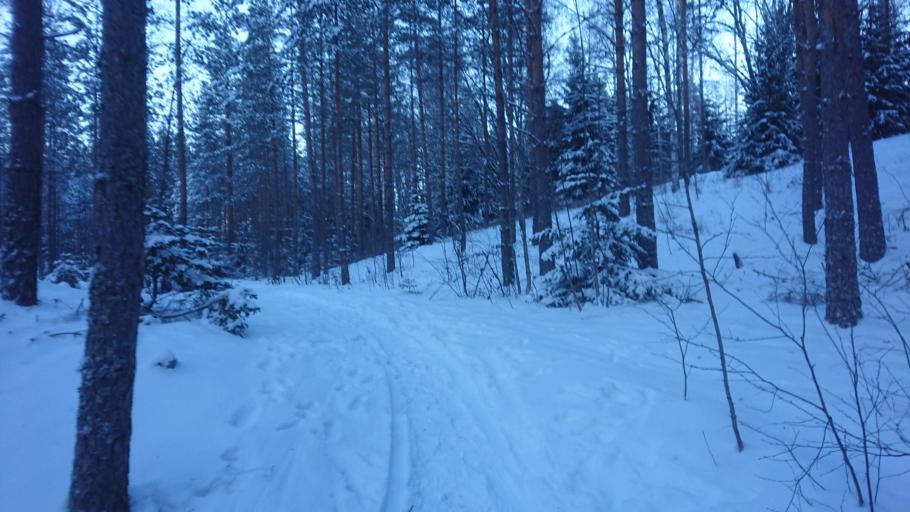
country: SE
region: Uppsala
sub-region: Uppsala Kommun
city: Gamla Uppsala
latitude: 59.9538
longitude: 17.5913
